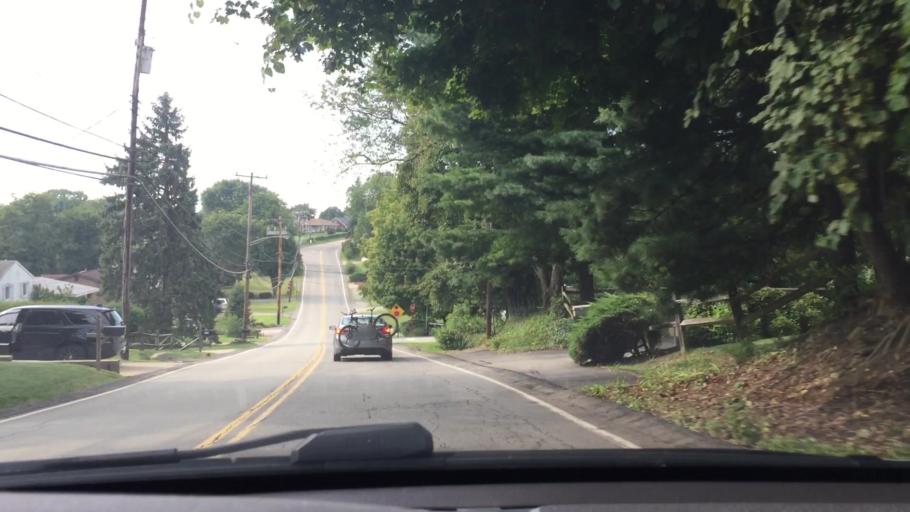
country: US
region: Pennsylvania
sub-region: Allegheny County
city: Pitcairn
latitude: 40.4211
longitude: -79.7478
